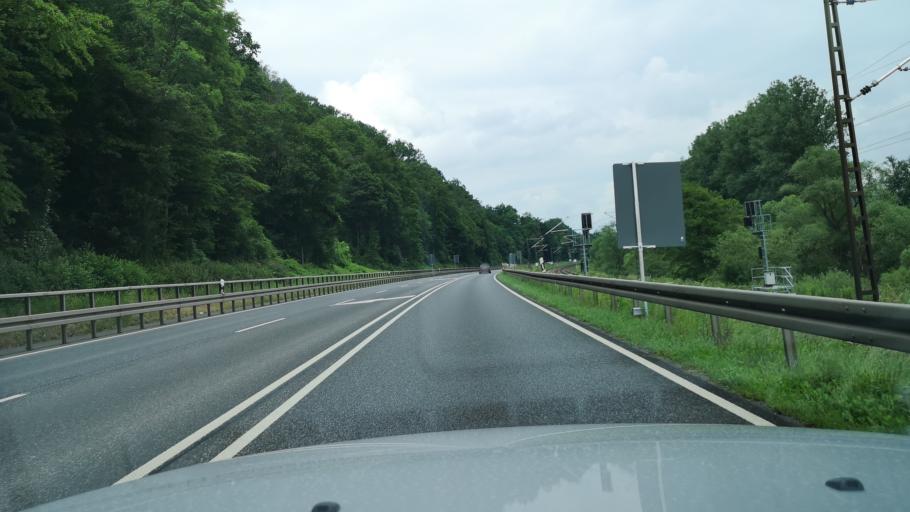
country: DE
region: Hesse
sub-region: Regierungsbezirk Kassel
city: Bad Hersfeld
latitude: 50.8887
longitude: 9.7279
